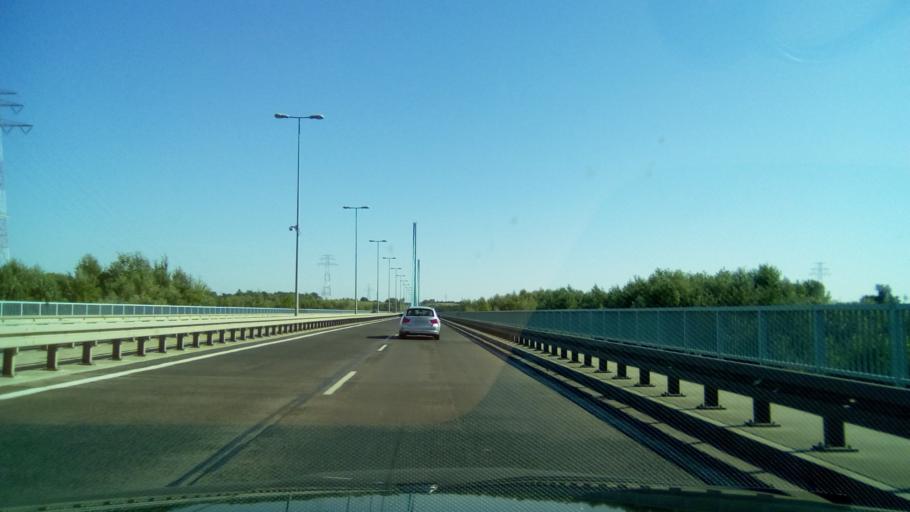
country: PL
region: Masovian Voivodeship
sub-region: Plock
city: Plock
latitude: 52.5156
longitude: 19.7218
